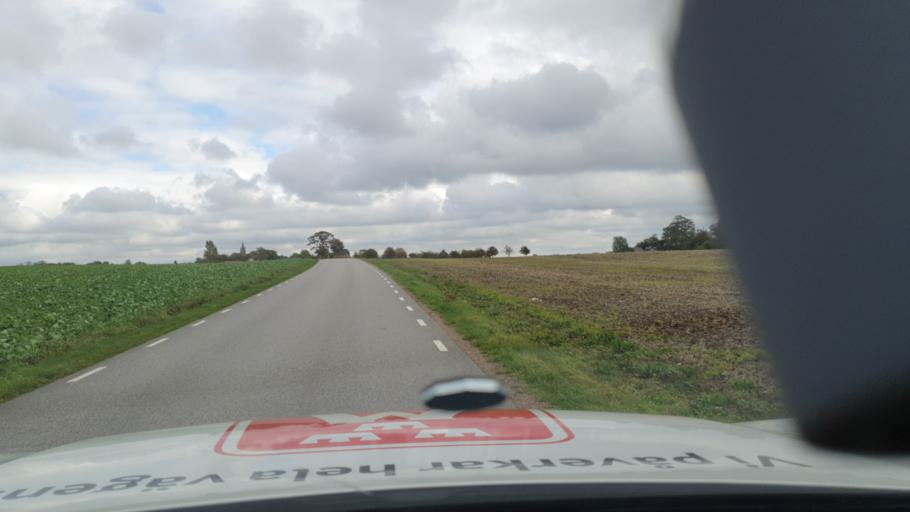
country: SE
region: Skane
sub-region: Vellinge Kommun
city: Vellinge
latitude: 55.4460
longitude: 13.0668
